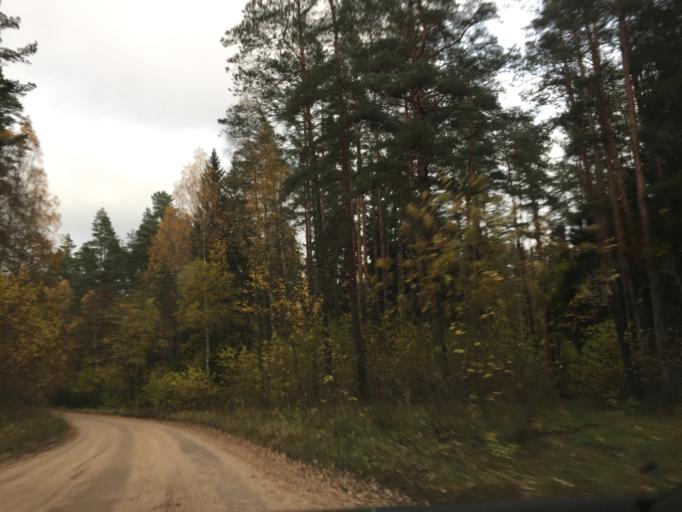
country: LV
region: Cesu Rajons
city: Cesis
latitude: 57.3406
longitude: 25.1564
